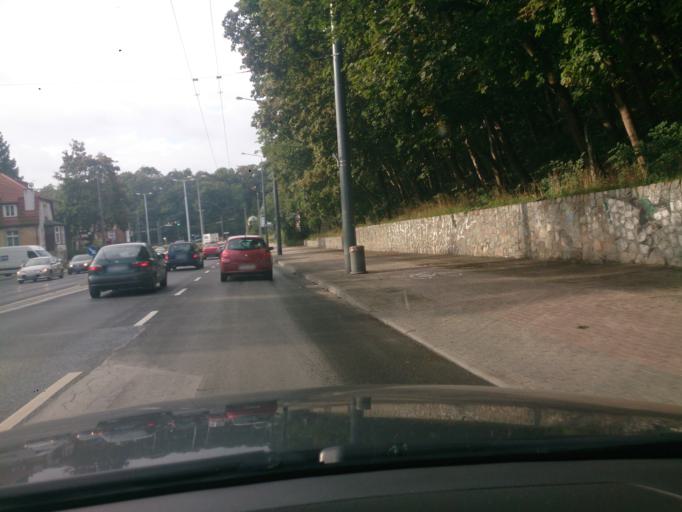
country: PL
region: Pomeranian Voivodeship
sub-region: Sopot
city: Sopot
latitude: 54.4516
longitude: 18.5550
